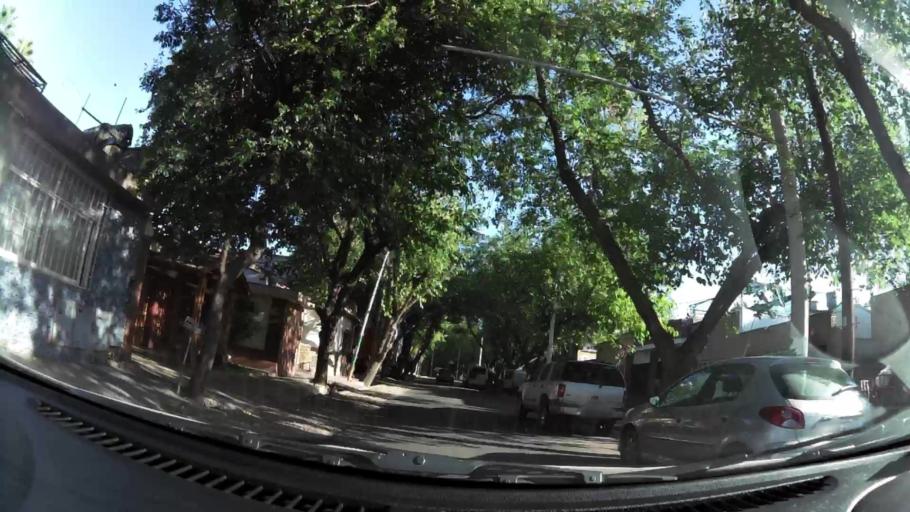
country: AR
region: Mendoza
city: Mendoza
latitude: -32.9092
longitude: -68.8287
